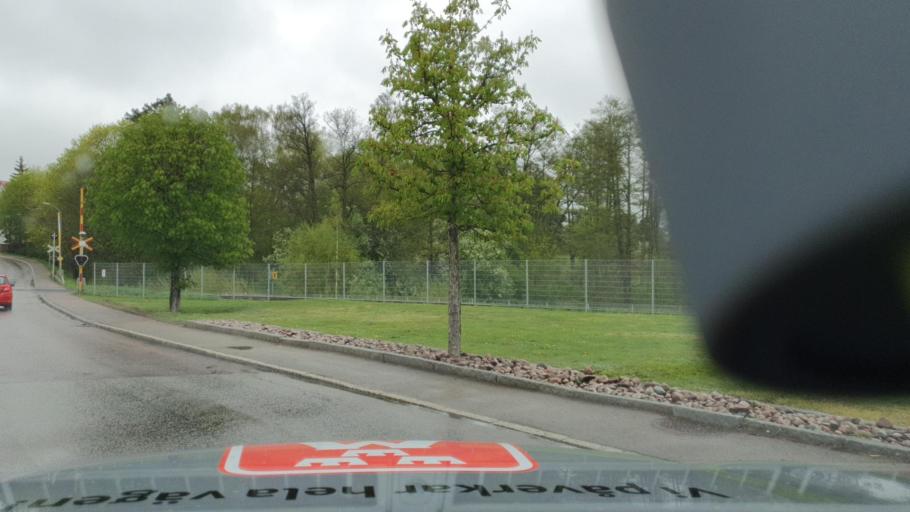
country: SE
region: Kalmar
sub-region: Hogsby Kommun
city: Hoegsby
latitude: 57.1670
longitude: 16.0255
